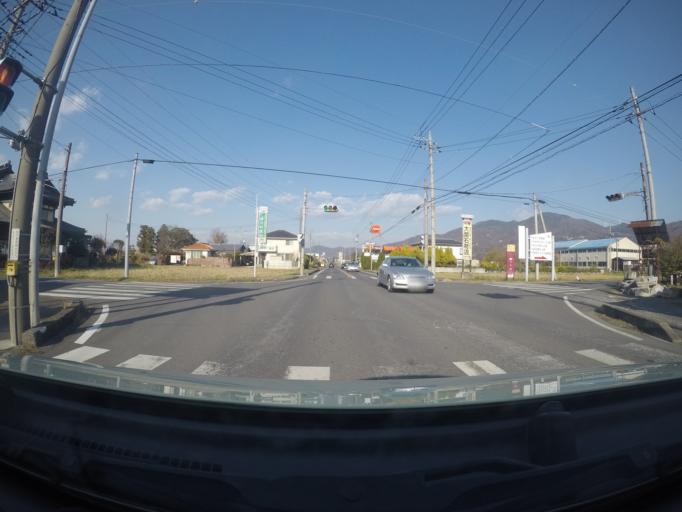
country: JP
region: Ibaraki
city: Makabe
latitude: 36.2772
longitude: 140.1071
